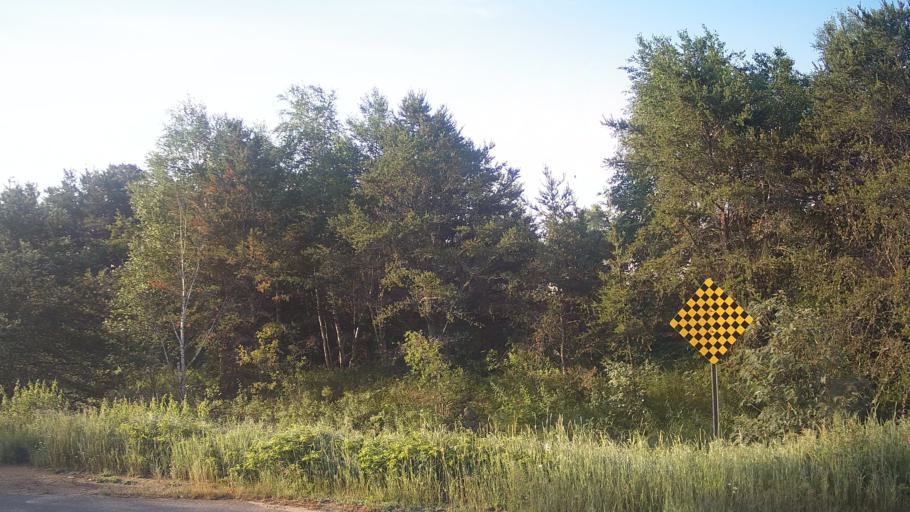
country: CA
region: Ontario
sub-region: Rainy River District
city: Atikokan
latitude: 49.4141
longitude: -91.6555
